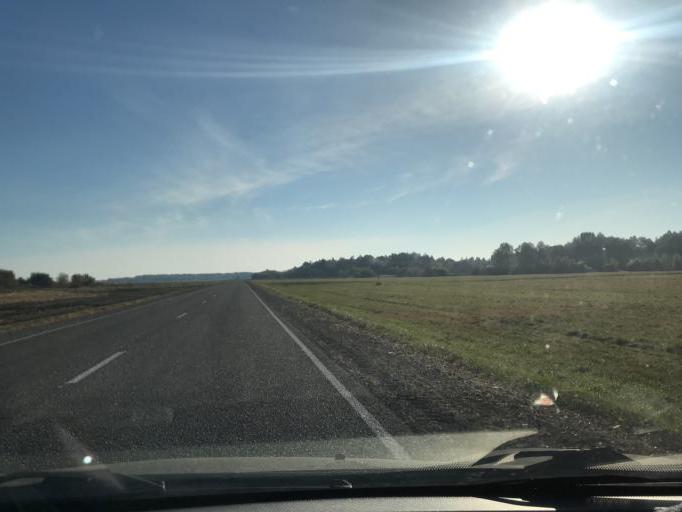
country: BY
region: Gomel
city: Brahin
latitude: 51.7738
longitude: 30.2670
